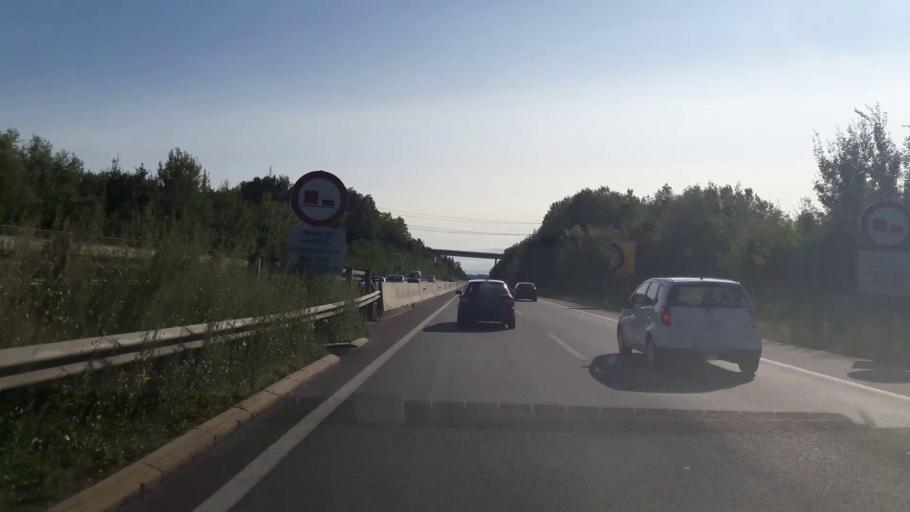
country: AT
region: Styria
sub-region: Politischer Bezirk Weiz
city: Nitscha
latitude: 47.1024
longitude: 15.7577
